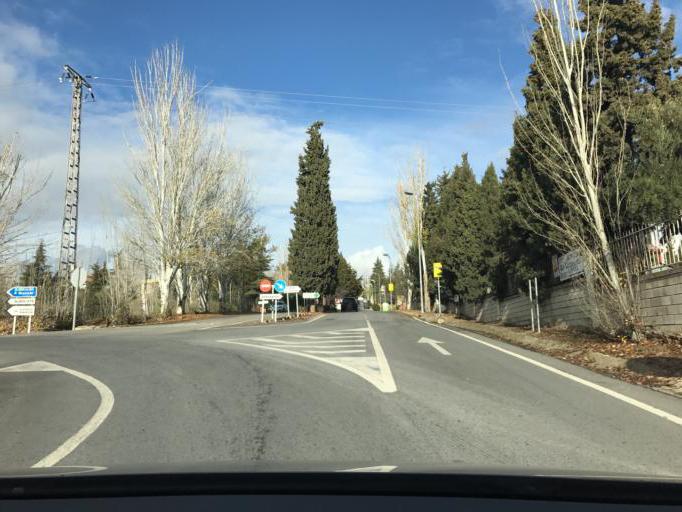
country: ES
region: Andalusia
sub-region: Provincia de Granada
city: Albolote
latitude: 37.2369
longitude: -3.6451
